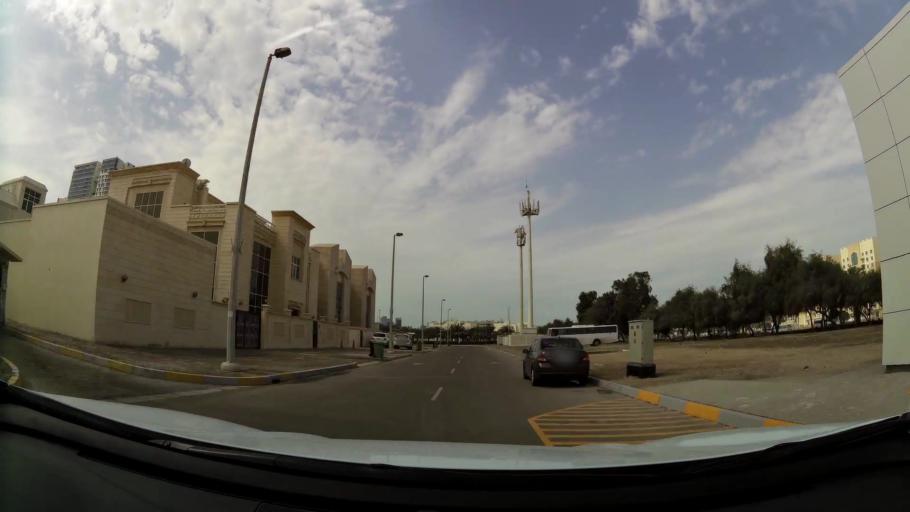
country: AE
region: Abu Dhabi
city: Abu Dhabi
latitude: 24.4158
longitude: 54.4667
